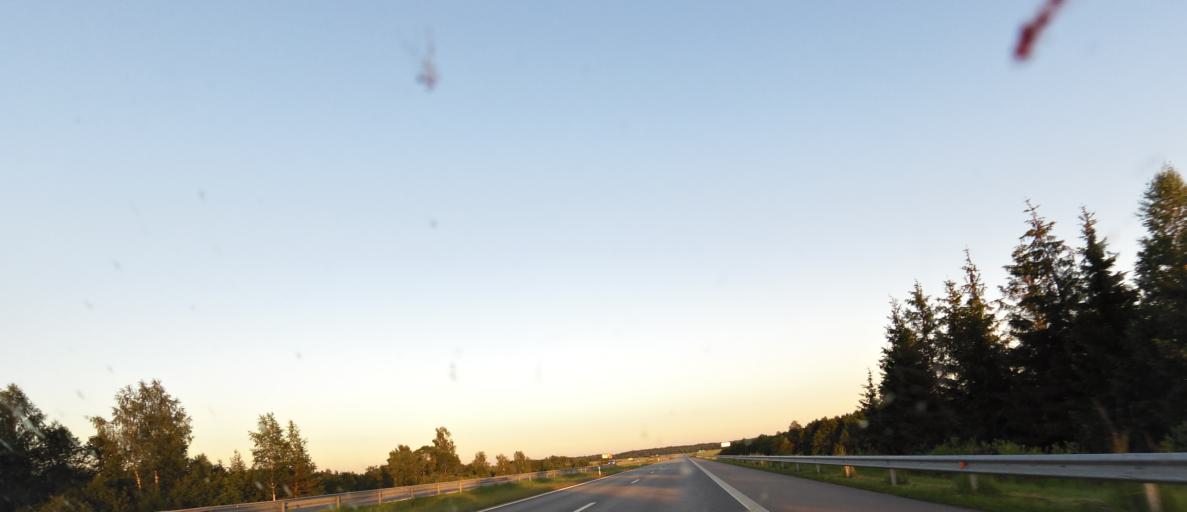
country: LT
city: Sirvintos
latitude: 54.9306
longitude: 24.9838
